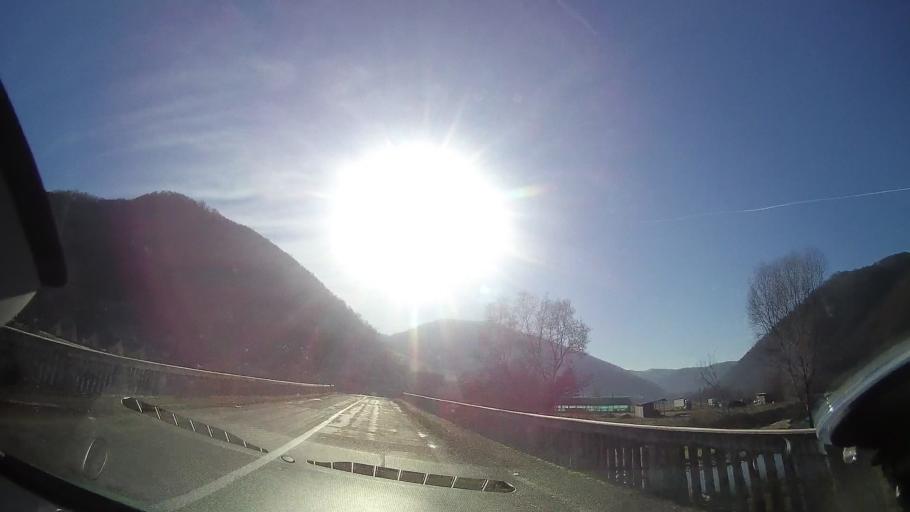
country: RO
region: Bihor
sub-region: Comuna Bulz
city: Bulz
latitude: 46.9479
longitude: 22.6749
